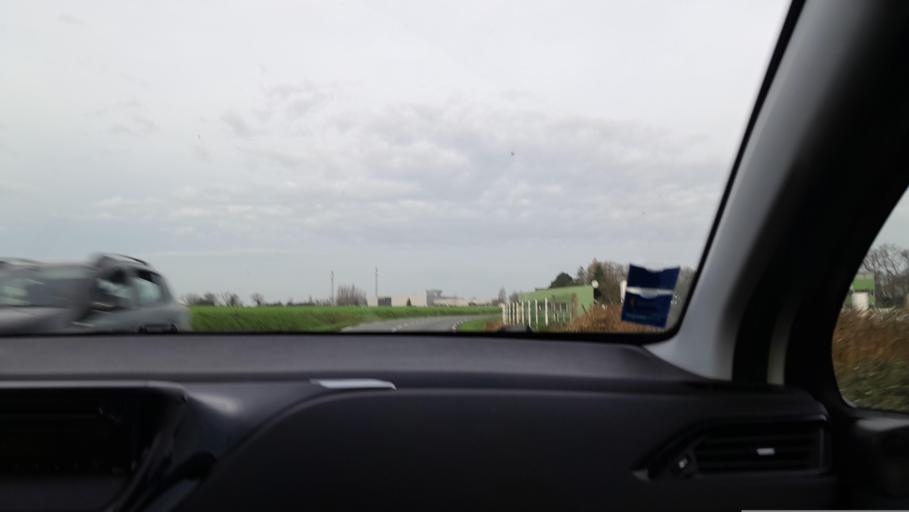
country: FR
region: Brittany
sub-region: Departement d'Ille-et-Vilaine
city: La Guerche-de-Bretagne
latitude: 47.9306
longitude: -1.2199
